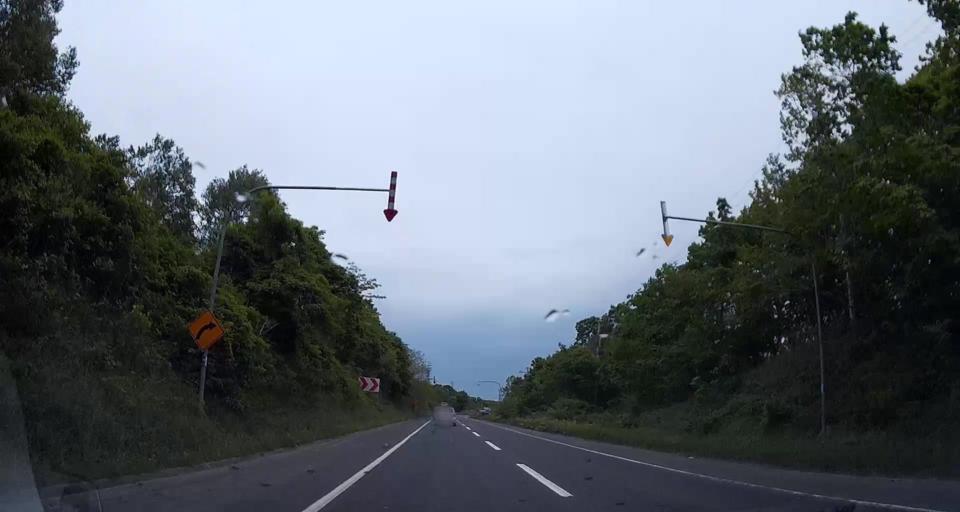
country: JP
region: Hokkaido
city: Chitose
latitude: 42.7010
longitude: 141.7422
